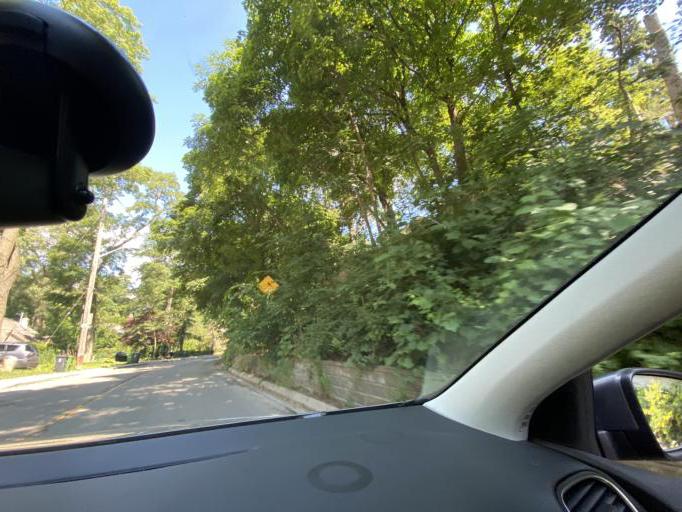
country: CA
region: Ontario
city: Etobicoke
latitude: 43.6547
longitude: -79.4926
